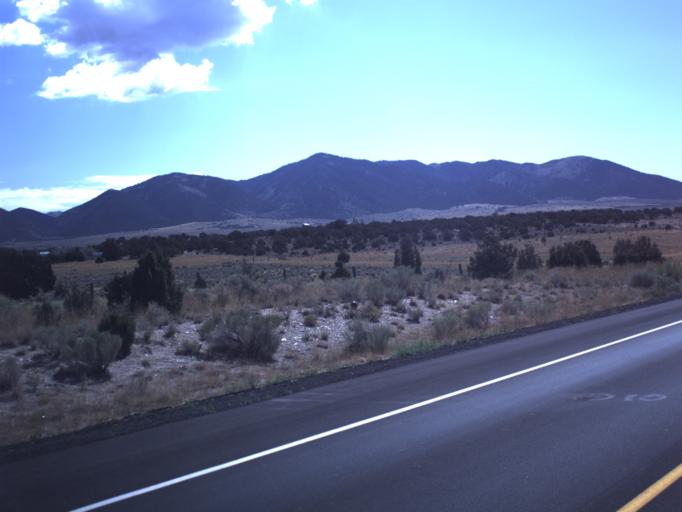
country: US
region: Utah
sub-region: Utah County
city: Eagle Mountain
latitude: 40.0428
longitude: -112.2914
